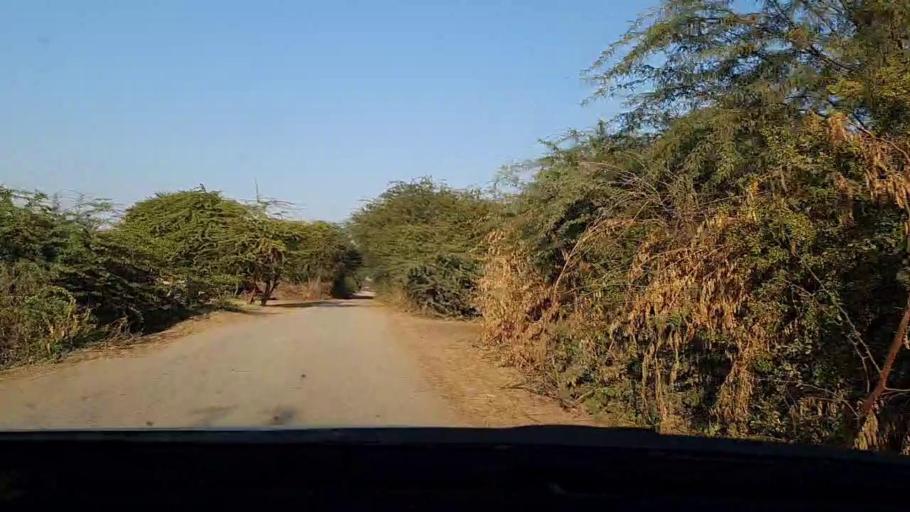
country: PK
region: Sindh
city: Tando Mittha Khan
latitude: 25.8647
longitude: 69.3059
